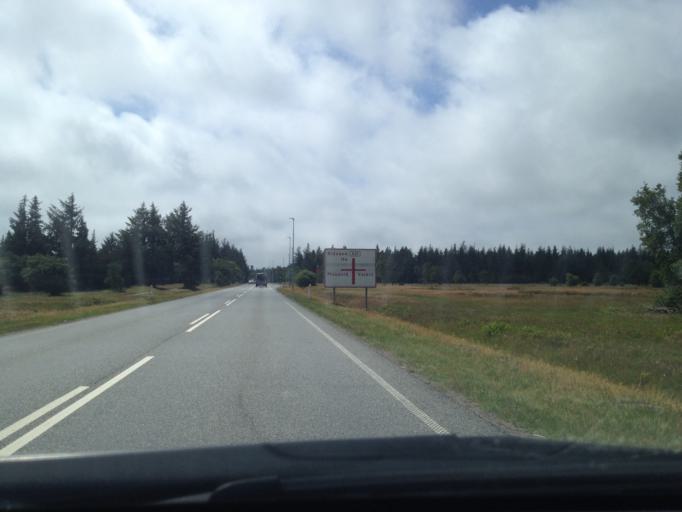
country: DK
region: South Denmark
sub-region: Varde Kommune
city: Oksbol
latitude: 55.6080
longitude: 8.2273
